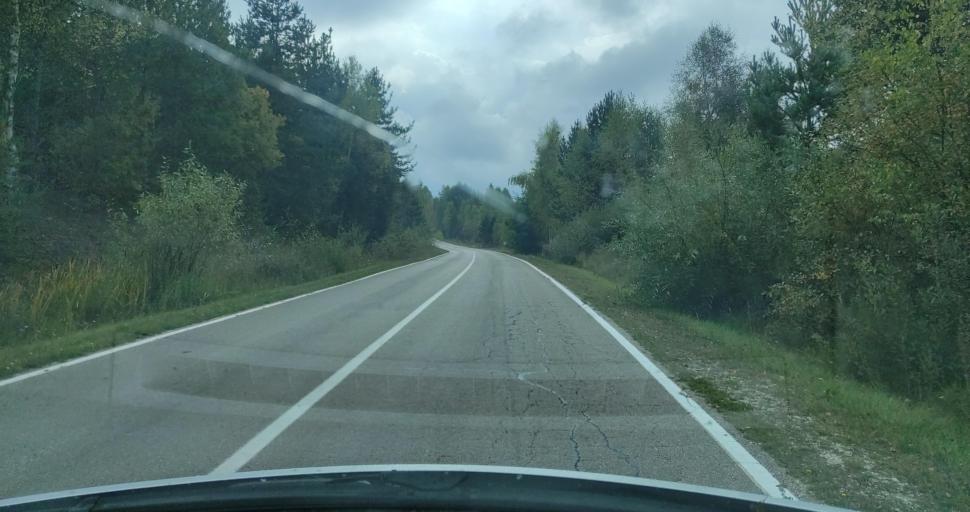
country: RS
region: Central Serbia
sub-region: Jablanicki Okrug
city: Crna Trava
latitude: 42.6912
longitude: 22.3182
